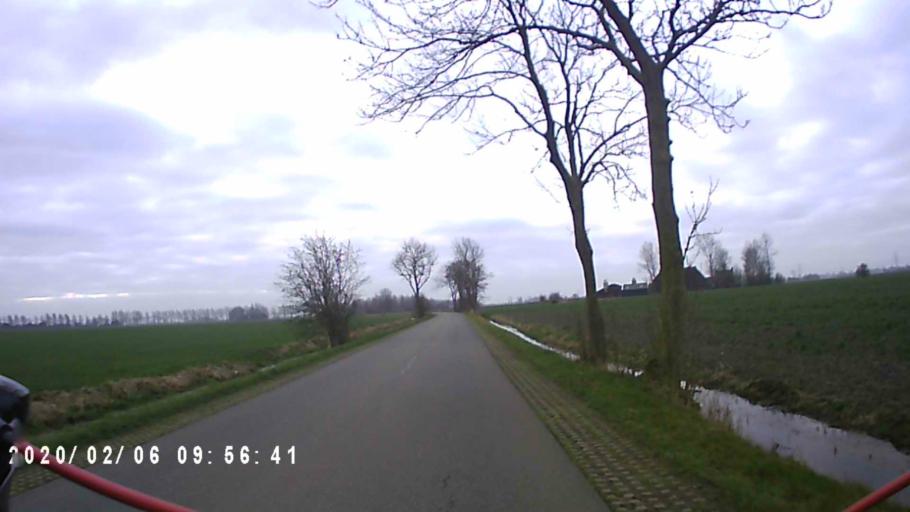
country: NL
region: Groningen
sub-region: Gemeente Zuidhorn
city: Aduard
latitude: 53.2770
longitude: 6.4977
